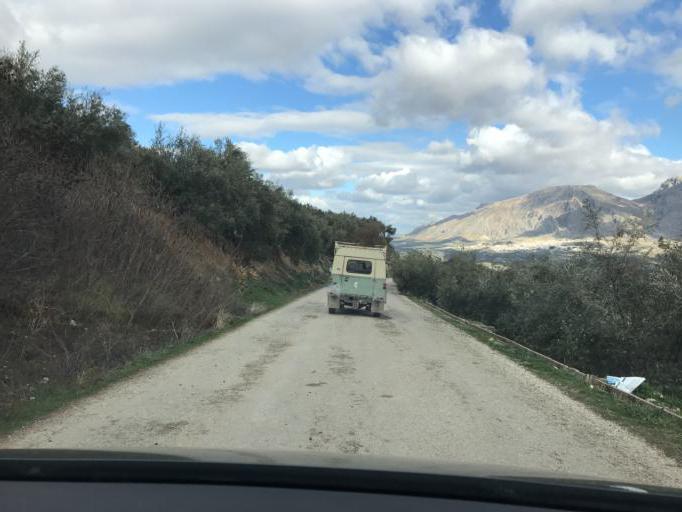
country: ES
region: Andalusia
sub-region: Provincia de Jaen
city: Jimena
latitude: 37.7991
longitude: -3.4646
